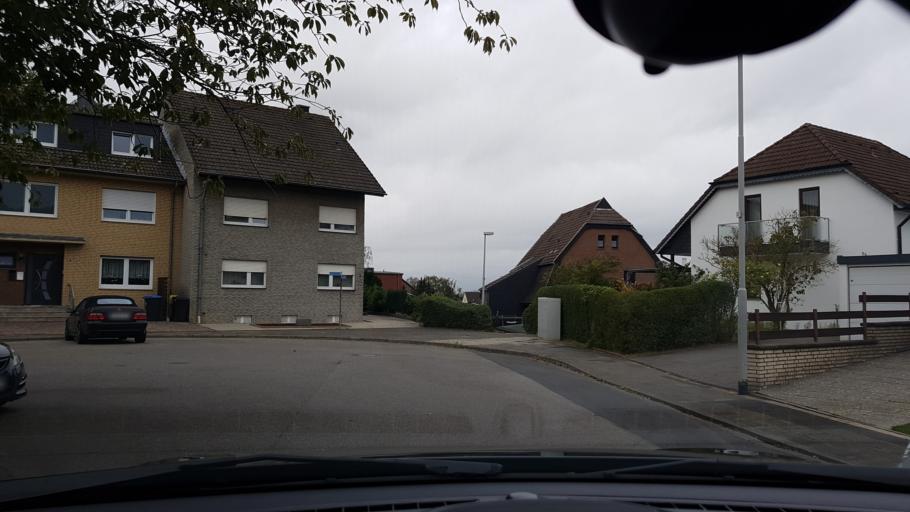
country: DE
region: North Rhine-Westphalia
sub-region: Regierungsbezirk Koln
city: Bedburg
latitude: 51.0368
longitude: 6.5972
